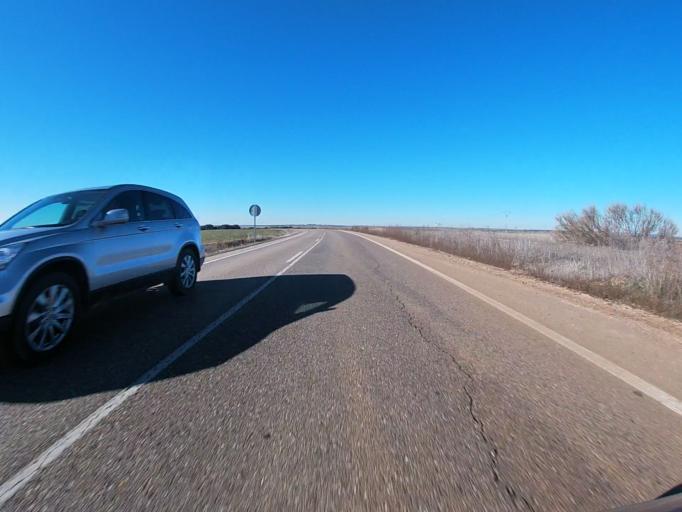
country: ES
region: Castille and Leon
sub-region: Provincia de Salamanca
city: Almenara de Tormes
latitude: 41.0750
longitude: -5.8351
